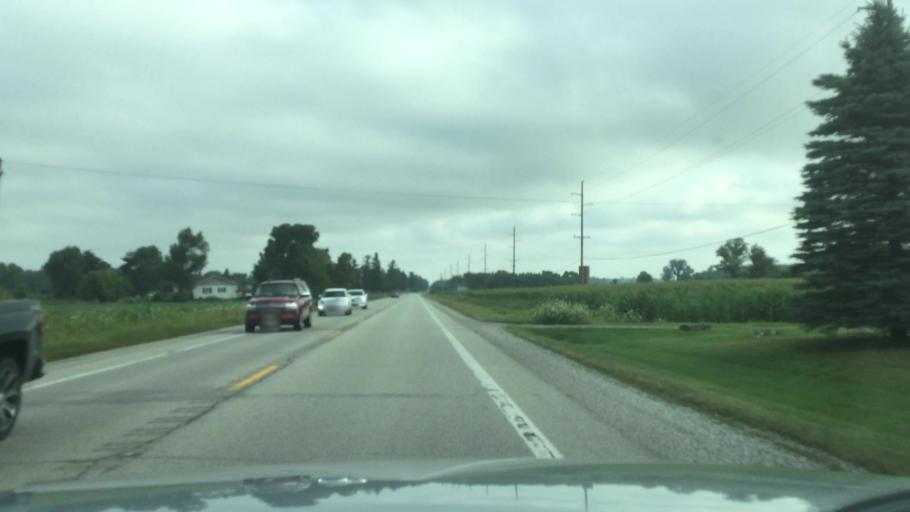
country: US
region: Michigan
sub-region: Saginaw County
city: Frankenmuth
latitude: 43.2732
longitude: -83.7357
